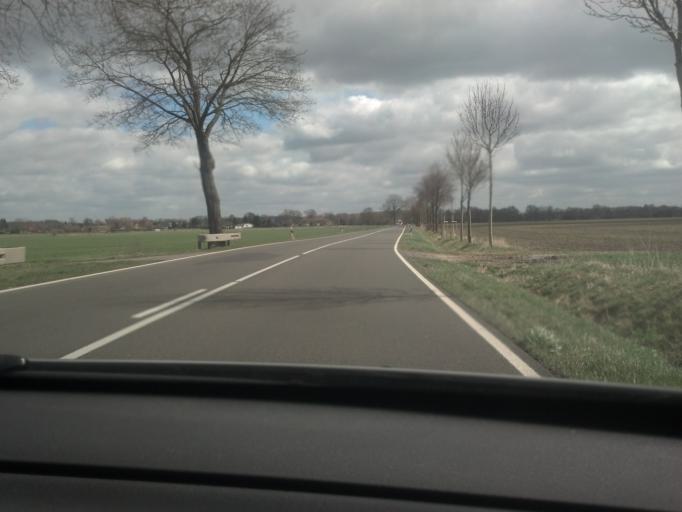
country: DE
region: Mecklenburg-Vorpommern
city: Rechlin
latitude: 53.3317
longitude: 12.6724
